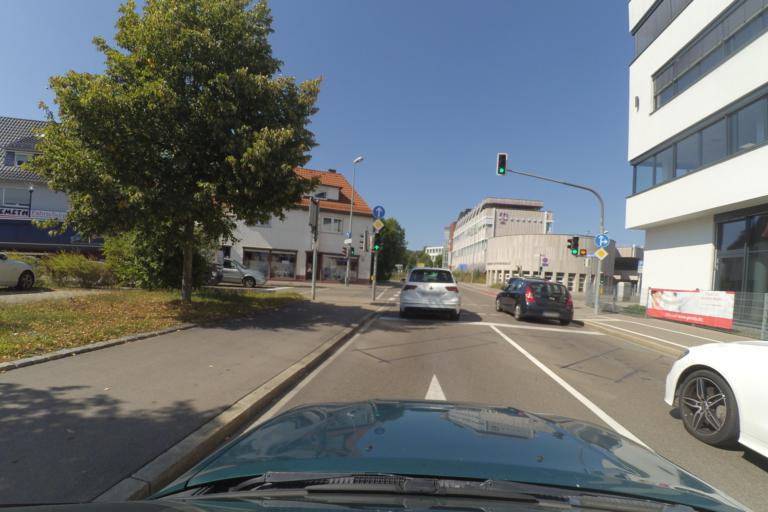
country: DE
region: Baden-Wuerttemberg
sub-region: Regierungsbezirk Stuttgart
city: Heidenheim an der Brenz
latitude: 48.6778
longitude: 10.1569
